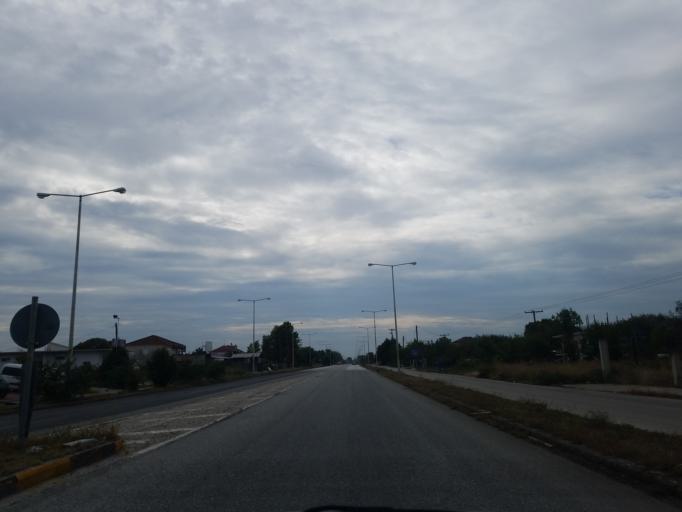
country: GR
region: Thessaly
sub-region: Trikala
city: Pyrgetos
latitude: 39.5841
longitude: 21.7395
